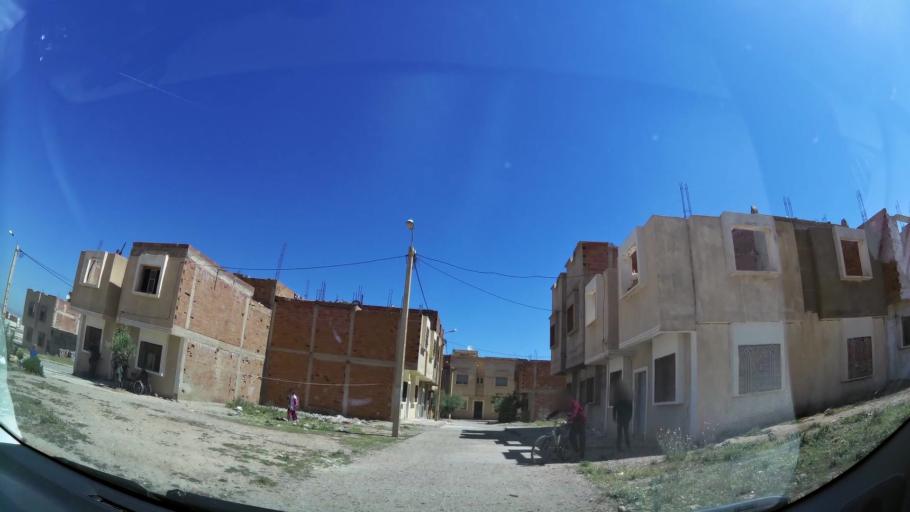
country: MA
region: Oriental
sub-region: Oujda-Angad
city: Oujda
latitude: 34.6553
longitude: -1.8759
